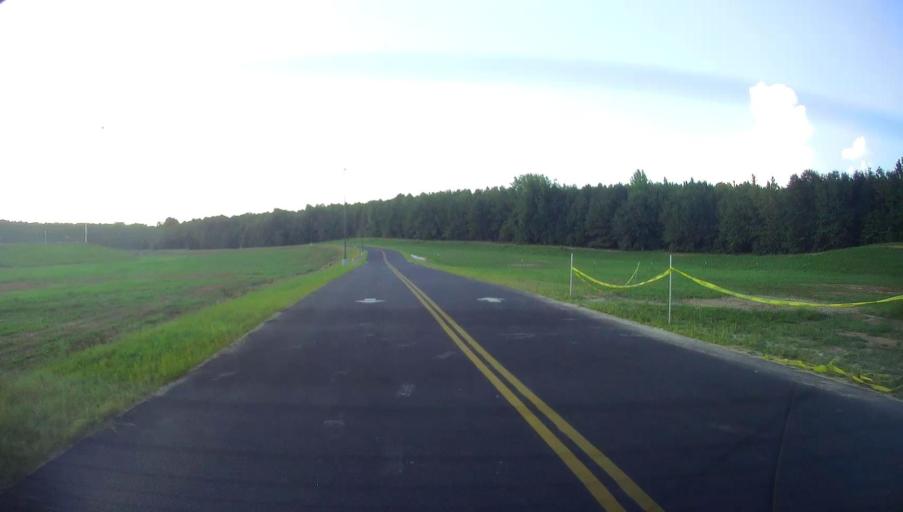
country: US
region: Georgia
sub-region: Peach County
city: Fort Valley
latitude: 32.5923
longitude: -83.8367
